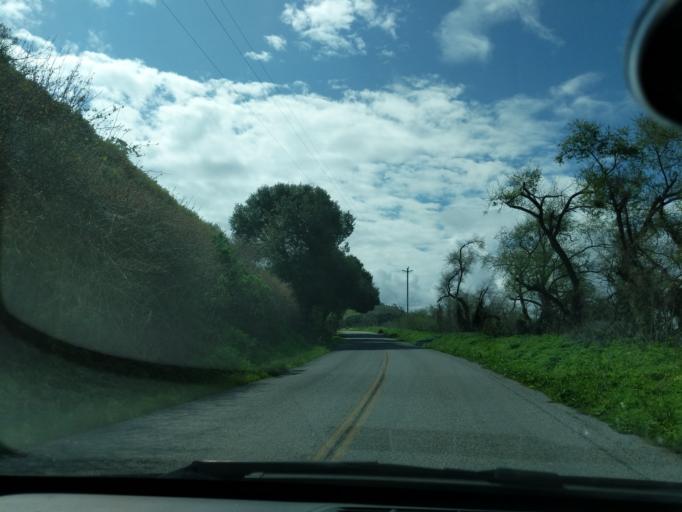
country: US
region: California
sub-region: Monterey County
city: Prunedale
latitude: 36.7661
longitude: -121.6022
